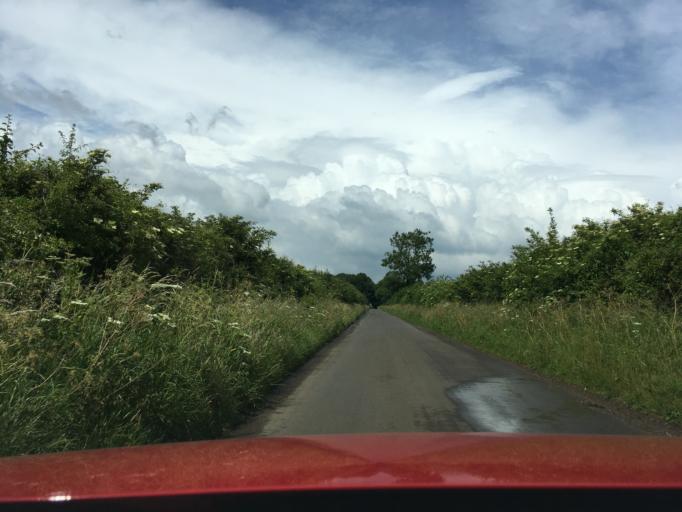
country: GB
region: England
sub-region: Gloucestershire
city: Tetbury
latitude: 51.6781
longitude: -2.1454
